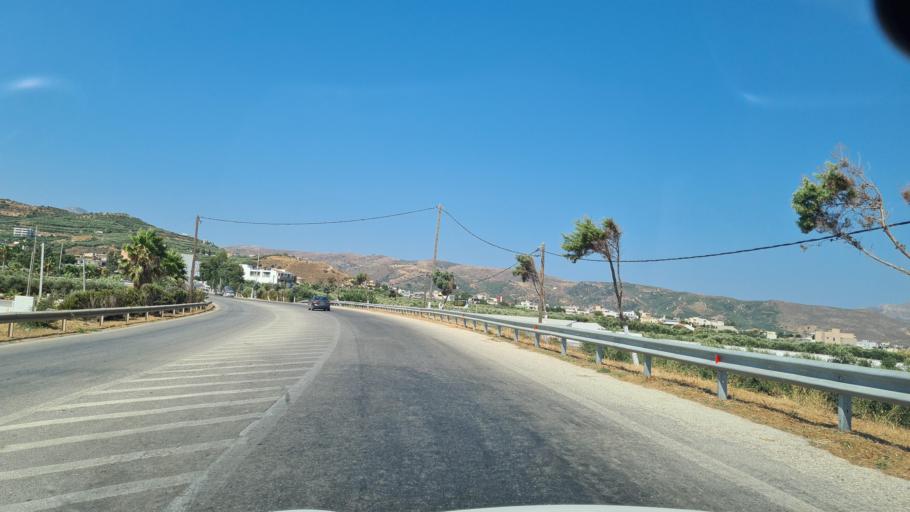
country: GR
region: Crete
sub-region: Nomos Chanias
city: Kissamos
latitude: 35.4938
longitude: 23.6714
